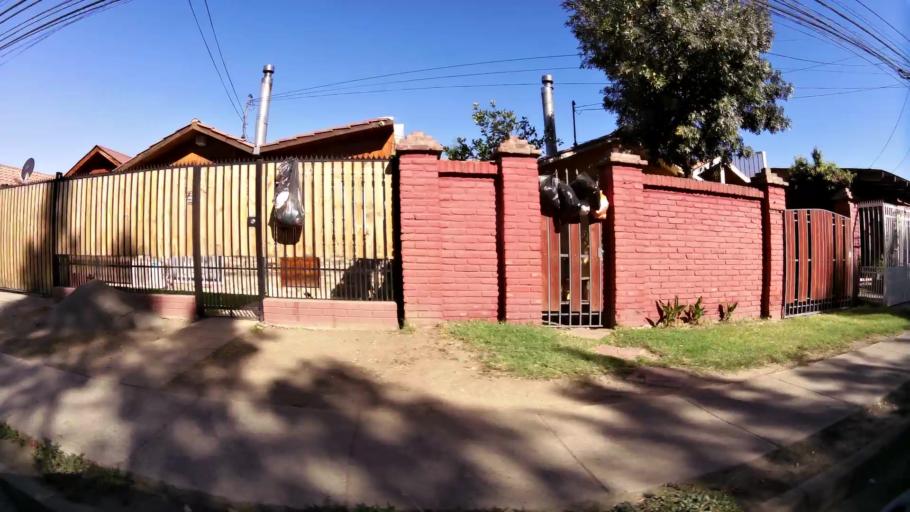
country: CL
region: O'Higgins
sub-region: Provincia de Cachapoal
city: Rancagua
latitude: -34.1805
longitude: -70.7682
